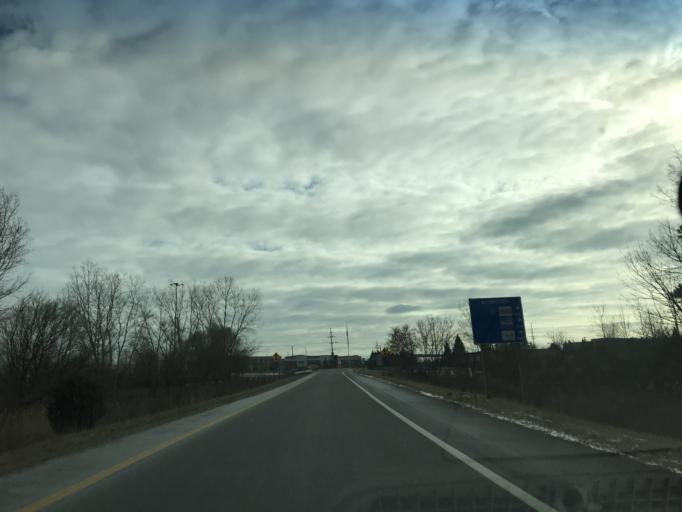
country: US
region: Michigan
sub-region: Oakland County
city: Pontiac
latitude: 42.7047
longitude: -83.3103
